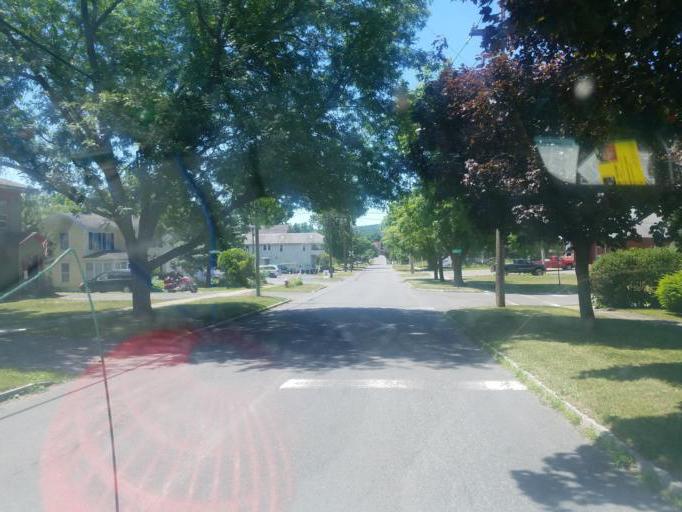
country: US
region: New York
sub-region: Yates County
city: Penn Yan
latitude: 42.6656
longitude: -77.0509
